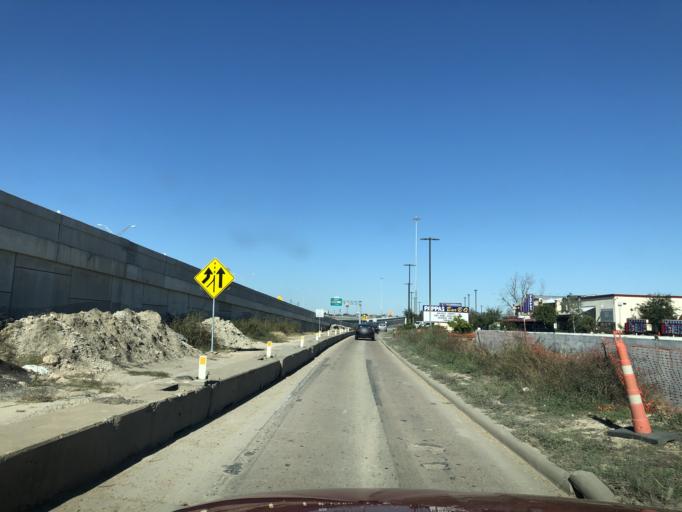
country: US
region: Texas
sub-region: Harris County
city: Deer Park
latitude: 29.6778
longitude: -95.1557
